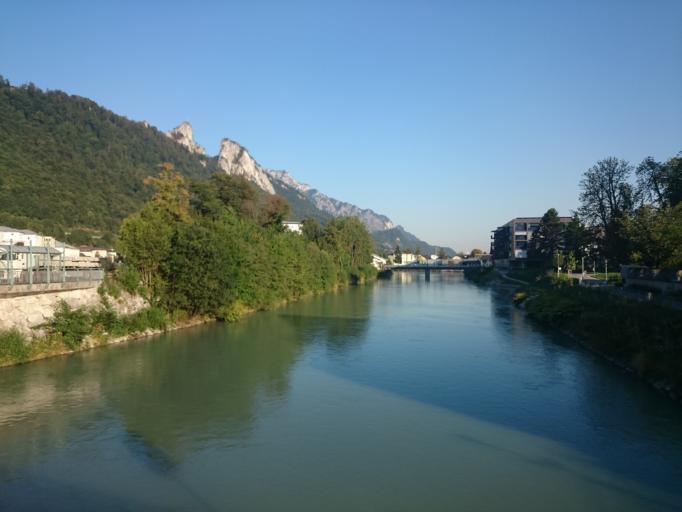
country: AT
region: Salzburg
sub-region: Politischer Bezirk Hallein
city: Hallein
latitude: 47.6832
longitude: 13.0971
